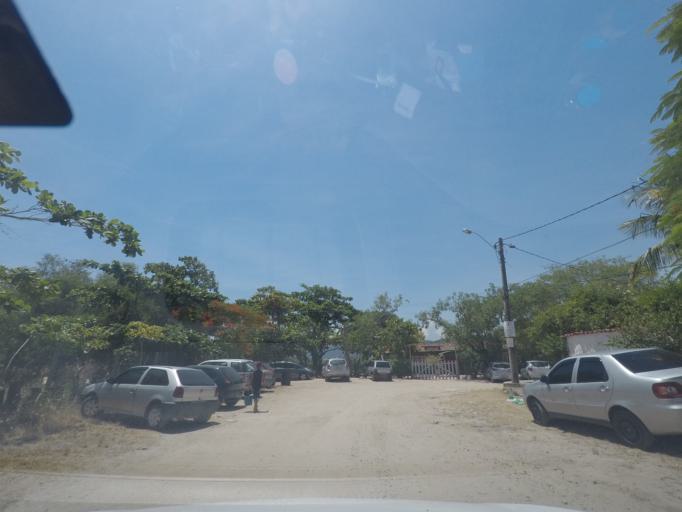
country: BR
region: Rio de Janeiro
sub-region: Niteroi
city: Niteroi
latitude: -22.9675
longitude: -43.0450
